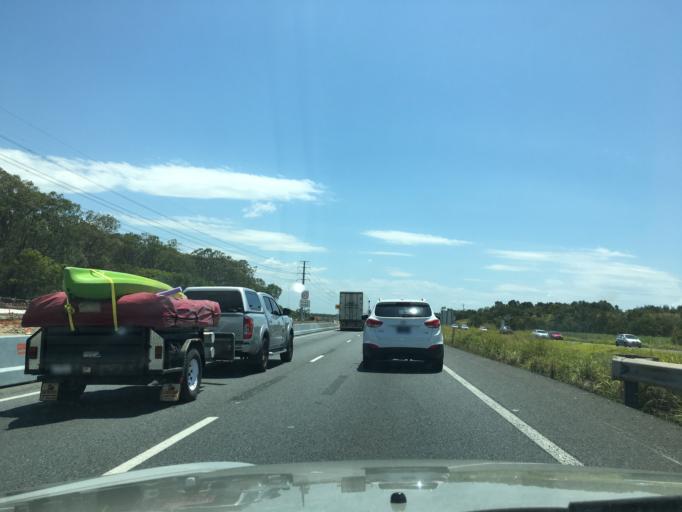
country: AU
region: Queensland
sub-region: Brisbane
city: Shorncliffe
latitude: -27.3643
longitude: 153.0971
